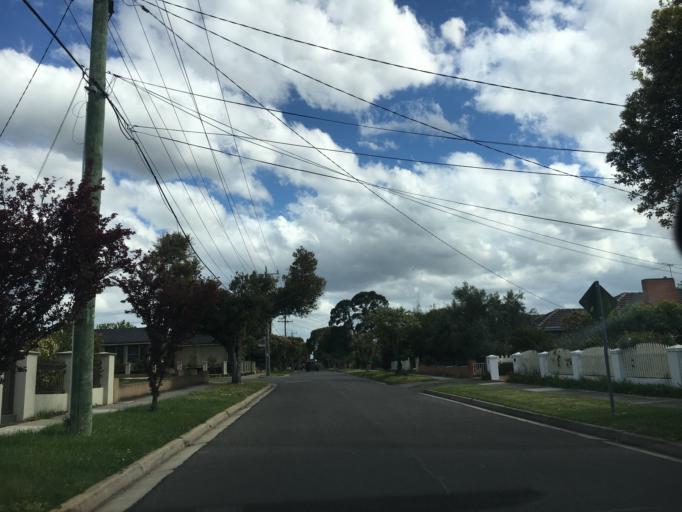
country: AU
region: Victoria
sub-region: Whitehorse
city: Vermont South
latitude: -37.8865
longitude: 145.1723
